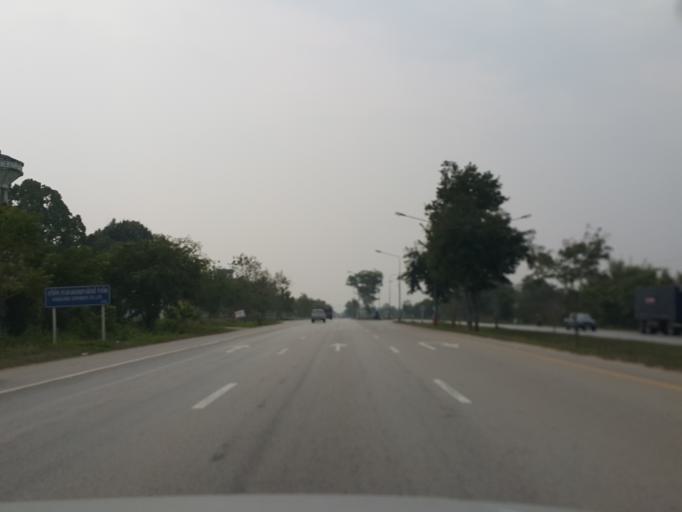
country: TH
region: Lampang
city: Ko Kha
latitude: 18.1713
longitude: 99.4070
